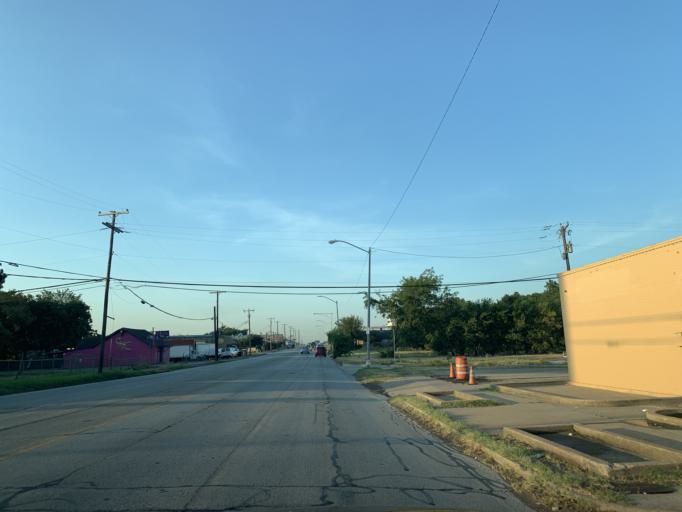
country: US
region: Texas
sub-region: Tarrant County
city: Blue Mound
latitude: 32.8101
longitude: -97.3516
